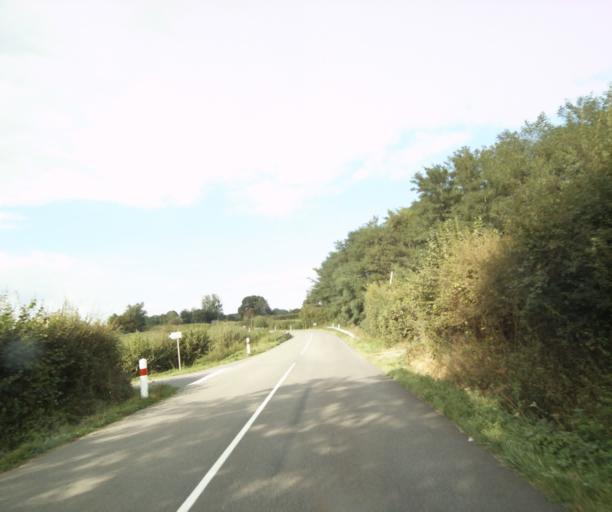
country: FR
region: Bourgogne
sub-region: Departement de Saone-et-Loire
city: Palinges
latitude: 46.5170
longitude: 4.2557
